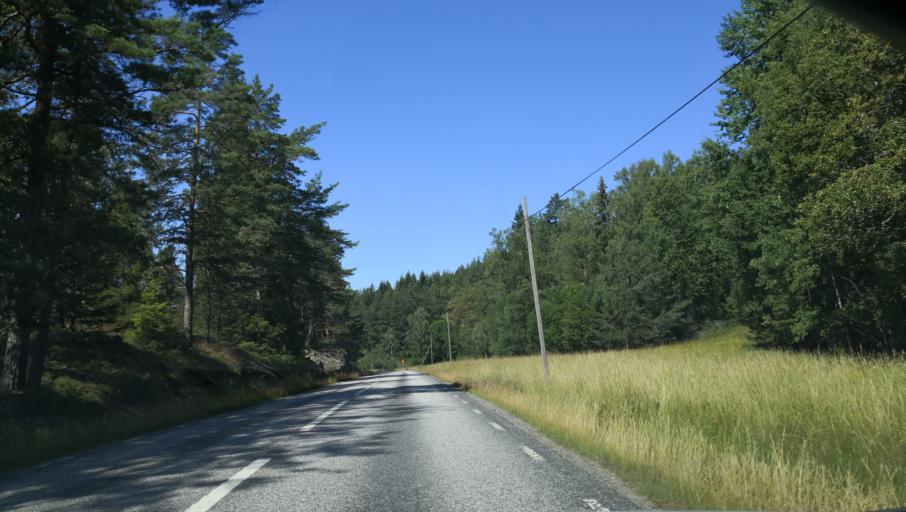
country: SE
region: Stockholm
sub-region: Varmdo Kommun
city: Hemmesta
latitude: 59.3948
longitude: 18.4819
